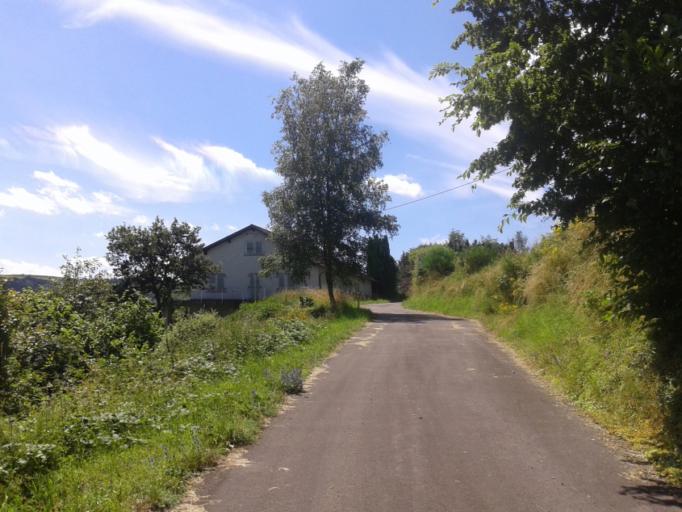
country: LU
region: Diekirch
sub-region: Canton de Diekirch
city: Bourscheid
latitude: 49.9312
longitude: 6.0647
